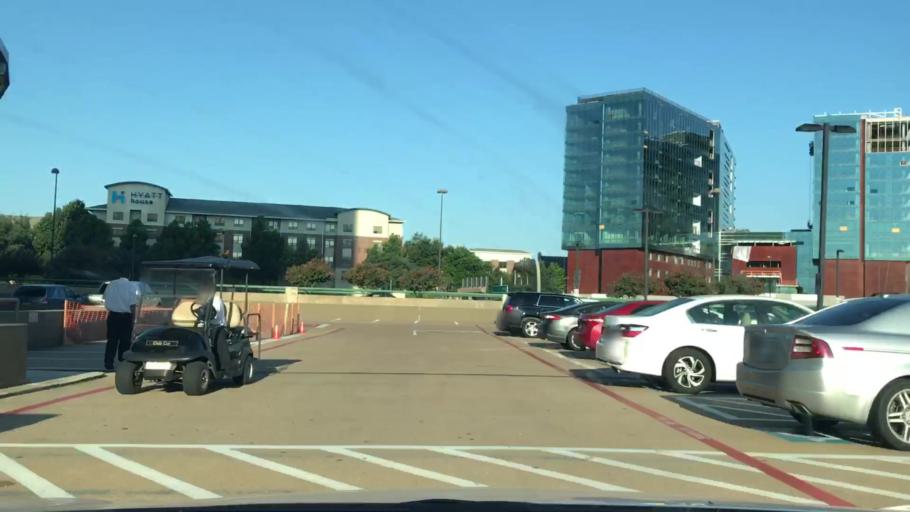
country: US
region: Texas
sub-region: Dallas County
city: University Park
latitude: 32.8623
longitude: -96.7691
